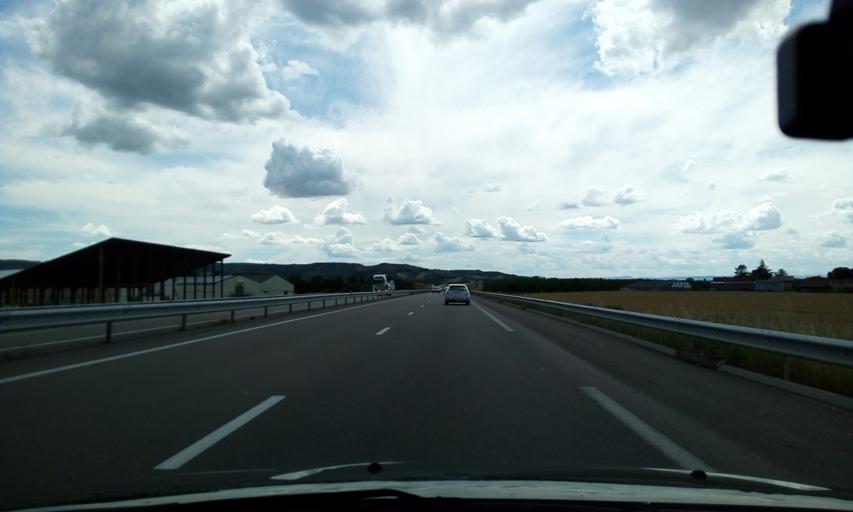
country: FR
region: Rhone-Alpes
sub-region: Departement de l'Isere
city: Saint-Lattier
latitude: 45.0620
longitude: 5.1967
